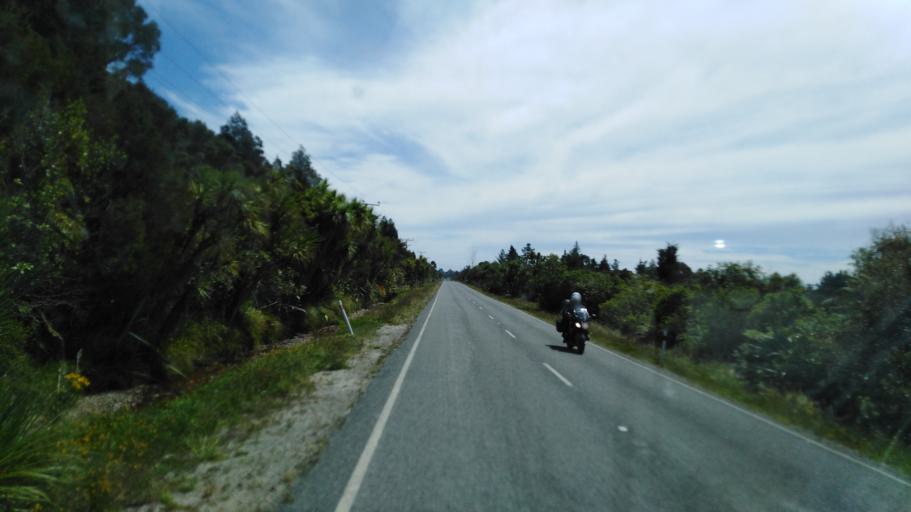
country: NZ
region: West Coast
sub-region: Buller District
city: Westport
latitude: -41.7434
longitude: 171.7151
